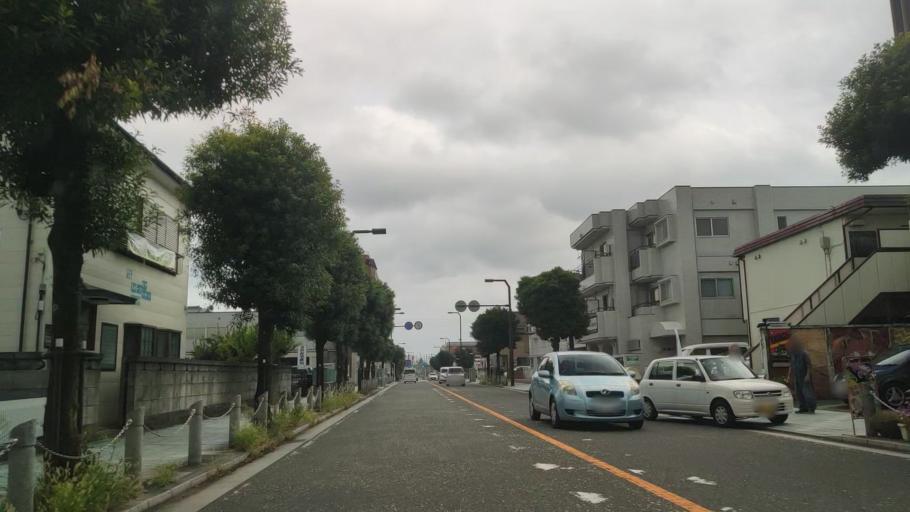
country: JP
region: Kanagawa
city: Minami-rinkan
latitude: 35.4637
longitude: 139.4609
